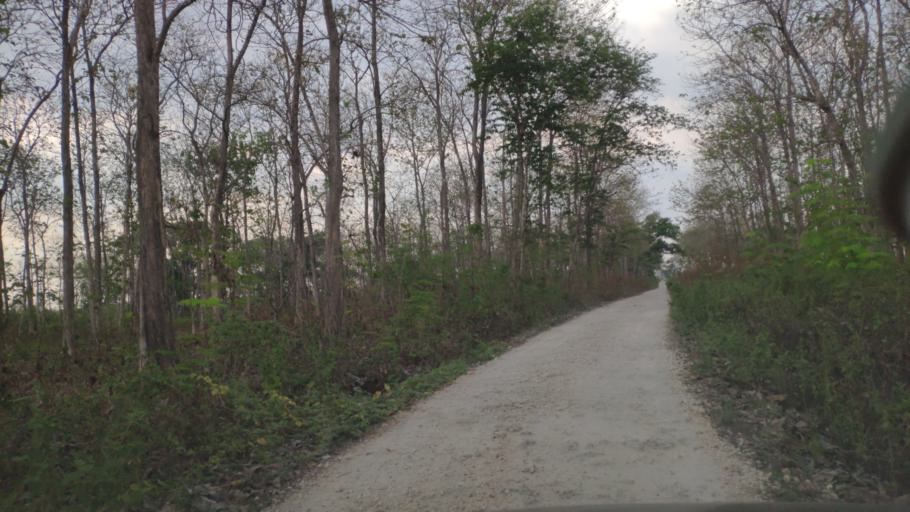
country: ID
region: Central Java
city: Randublatung
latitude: -7.2887
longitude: 111.2968
